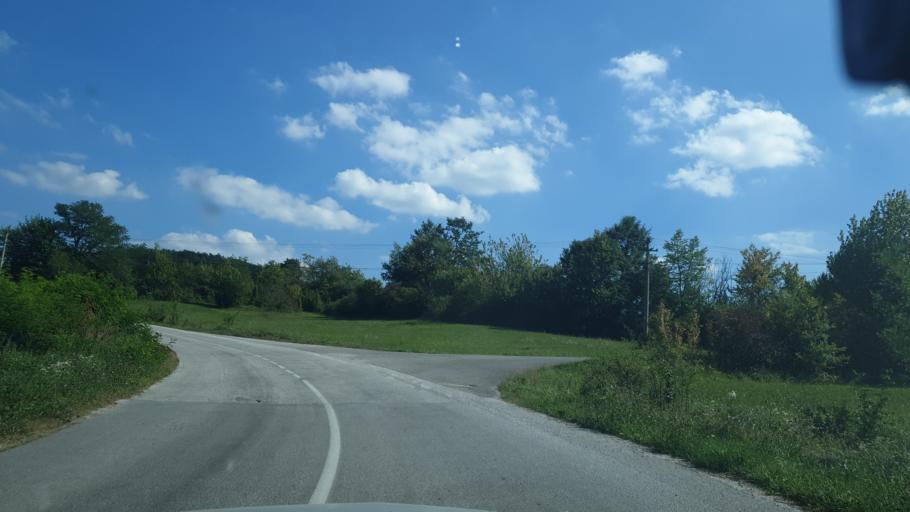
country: RS
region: Central Serbia
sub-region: Zlatiborski Okrug
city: Kosjeric
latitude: 44.0228
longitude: 20.0217
